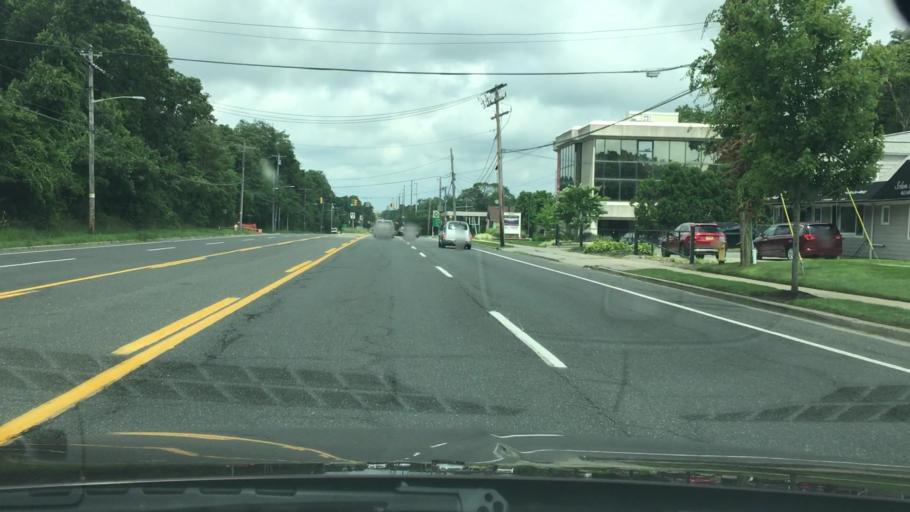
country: US
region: New York
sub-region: Suffolk County
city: Commack
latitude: 40.8132
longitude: -73.2940
